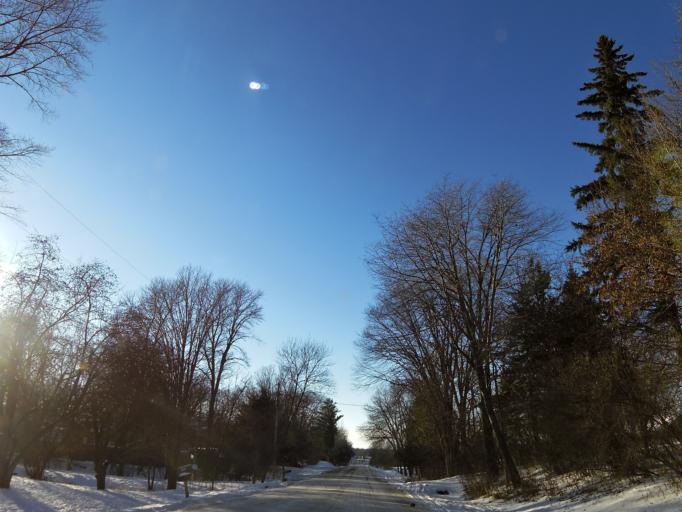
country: US
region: Minnesota
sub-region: Hennepin County
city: Mound
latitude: 44.9568
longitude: -93.6778
